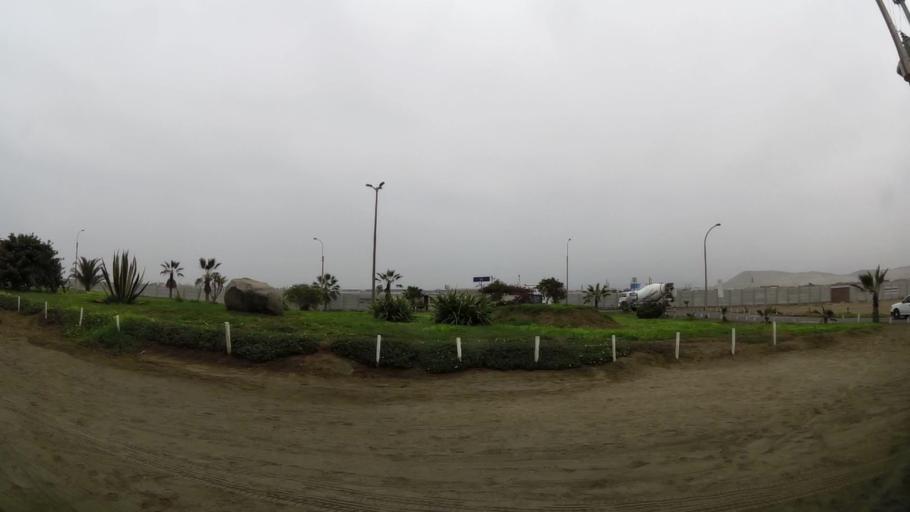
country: PE
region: Lima
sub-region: Lima
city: Punta Hermosa
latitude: -12.3283
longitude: -76.8315
